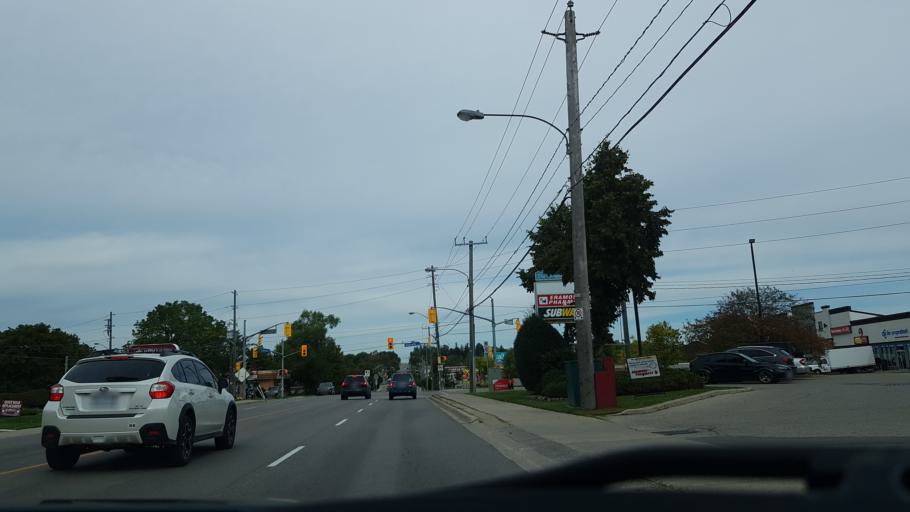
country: CA
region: Ontario
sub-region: Wellington County
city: Guelph
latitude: 43.5564
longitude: -80.2494
